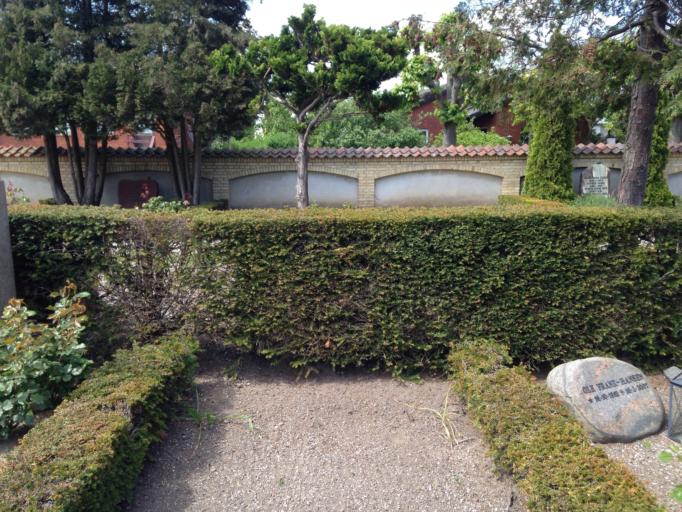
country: DK
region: Capital Region
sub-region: Hvidovre Kommune
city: Hvidovre
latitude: 55.6567
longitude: 12.4703
